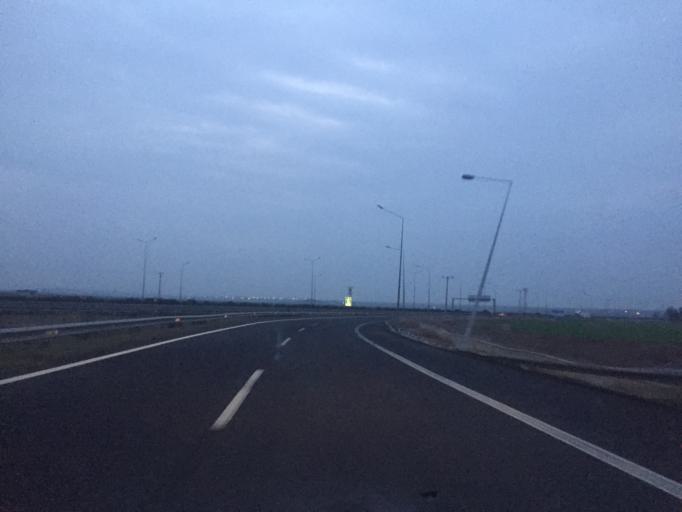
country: TR
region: Sanliurfa
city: Camlidere
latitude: 37.1596
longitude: 39.0171
